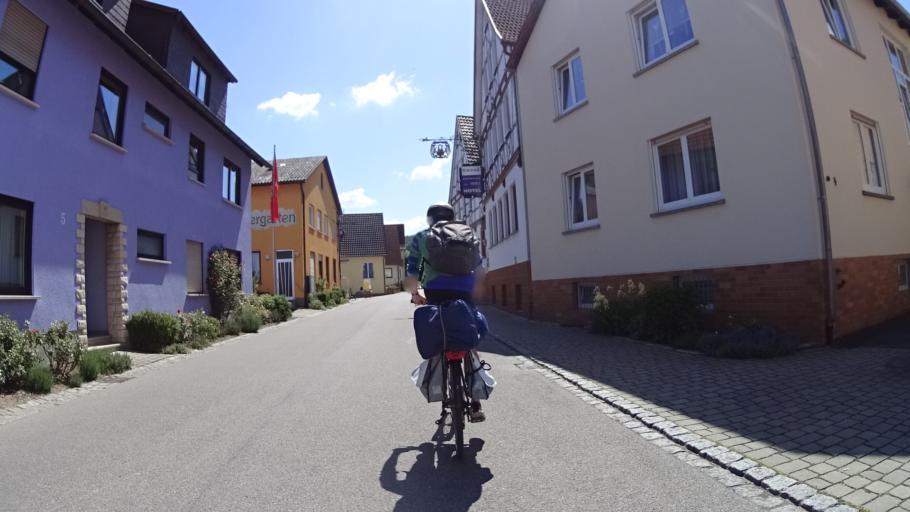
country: DE
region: Bavaria
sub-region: Regierungsbezirk Unterfranken
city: Tauberrettersheim
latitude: 49.4953
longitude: 9.9361
